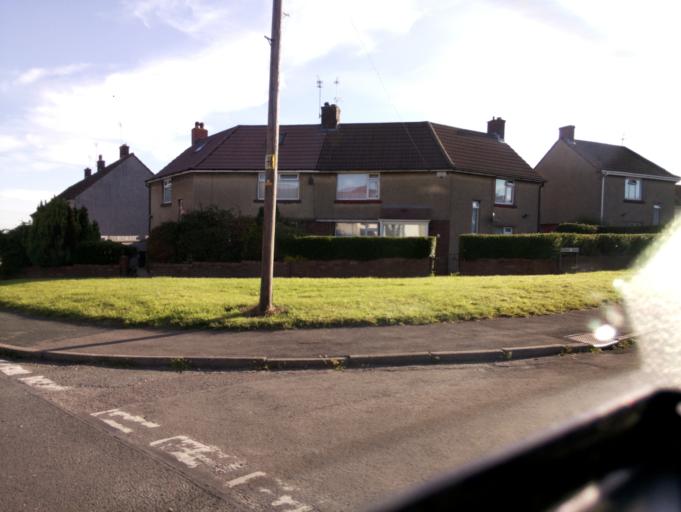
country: GB
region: England
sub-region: South Gloucestershire
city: Mangotsfield
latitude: 51.4850
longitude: -2.4909
